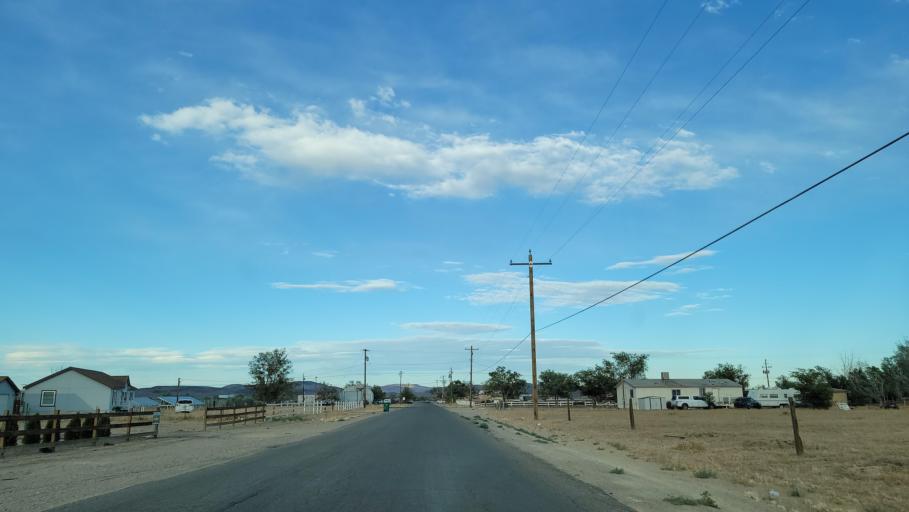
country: US
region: Nevada
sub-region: Lyon County
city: Silver Springs
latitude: 39.4007
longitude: -119.2326
